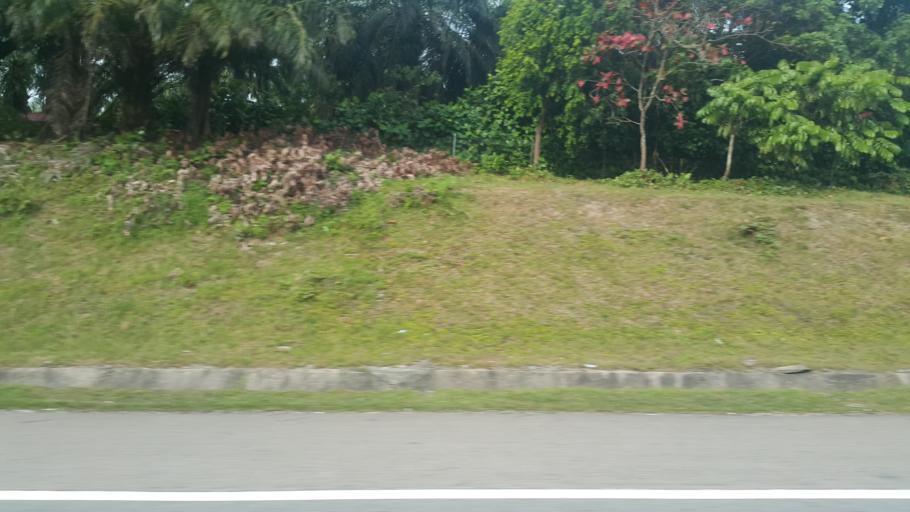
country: MY
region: Johor
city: Pekan Nenas
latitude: 1.3877
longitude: 103.5921
